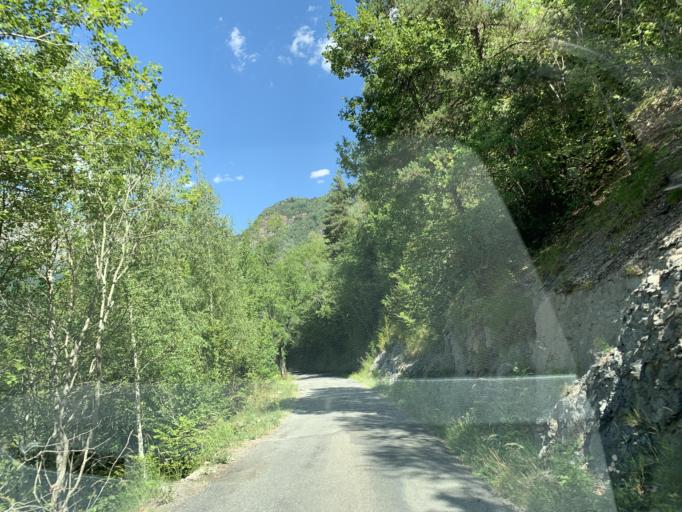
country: ES
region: Aragon
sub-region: Provincia de Huesca
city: Hoz de Jaca
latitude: 42.6959
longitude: -0.3083
